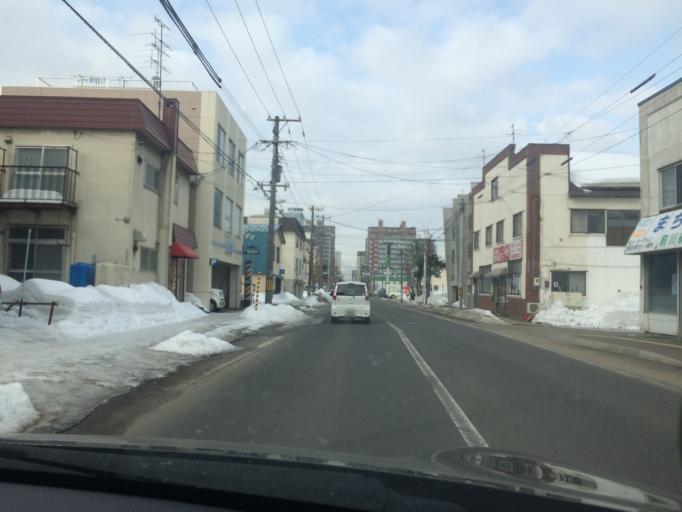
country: JP
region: Hokkaido
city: Sapporo
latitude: 43.0732
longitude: 141.3627
